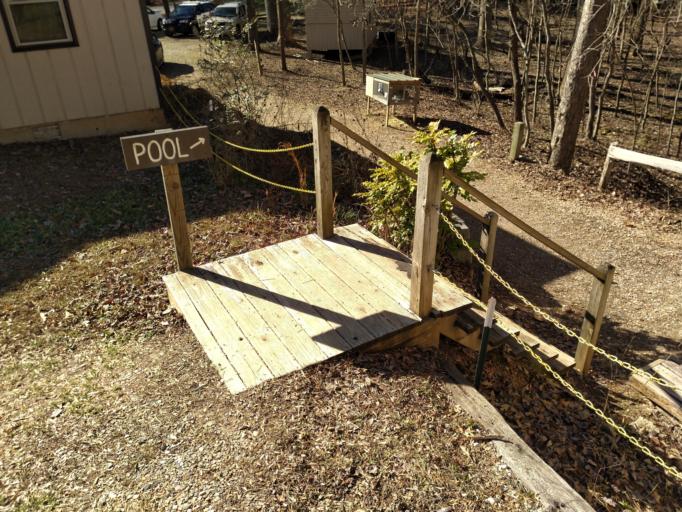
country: US
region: Virginia
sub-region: Buckingham County
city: Buckingham
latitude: 37.3903
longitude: -78.6406
